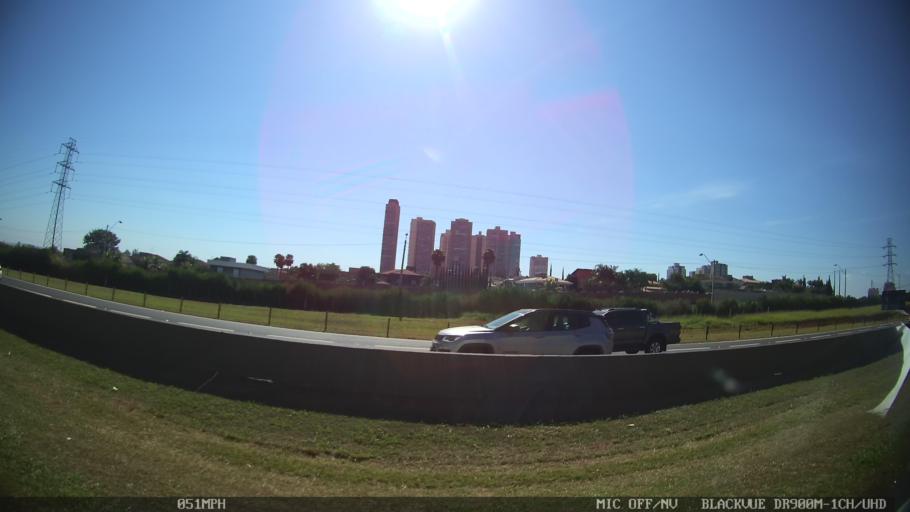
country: BR
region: Sao Paulo
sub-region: Ribeirao Preto
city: Ribeirao Preto
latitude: -21.2242
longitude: -47.8035
